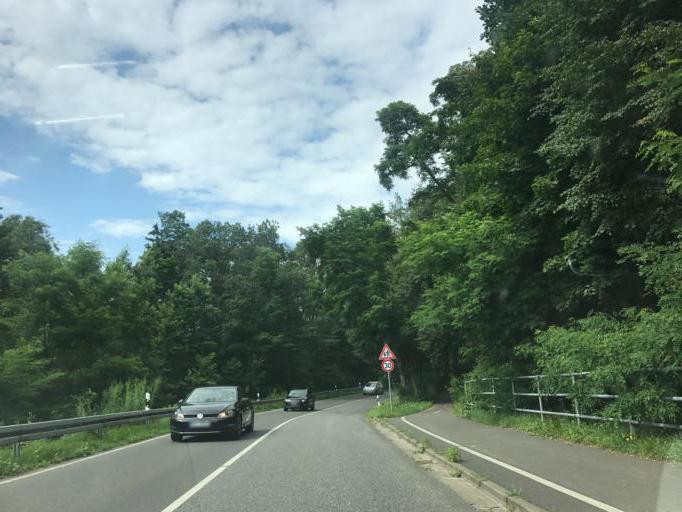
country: DE
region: Brandenburg
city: Rheinsberg
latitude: 53.1752
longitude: 12.8859
